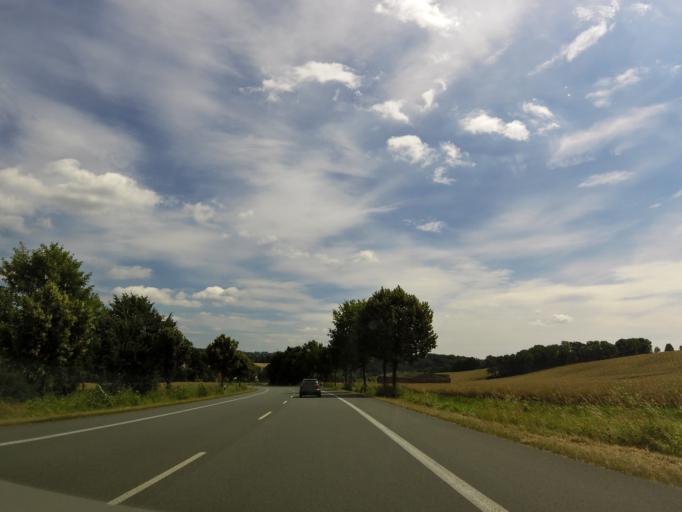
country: DE
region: North Rhine-Westphalia
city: Beverungen
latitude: 51.6346
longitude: 9.4039
